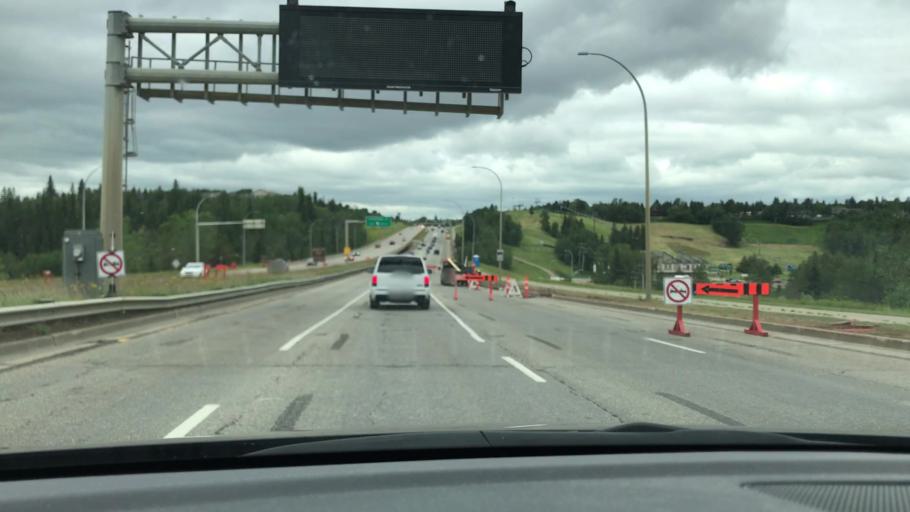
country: CA
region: Alberta
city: Edmonton
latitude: 53.4827
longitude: -113.5500
